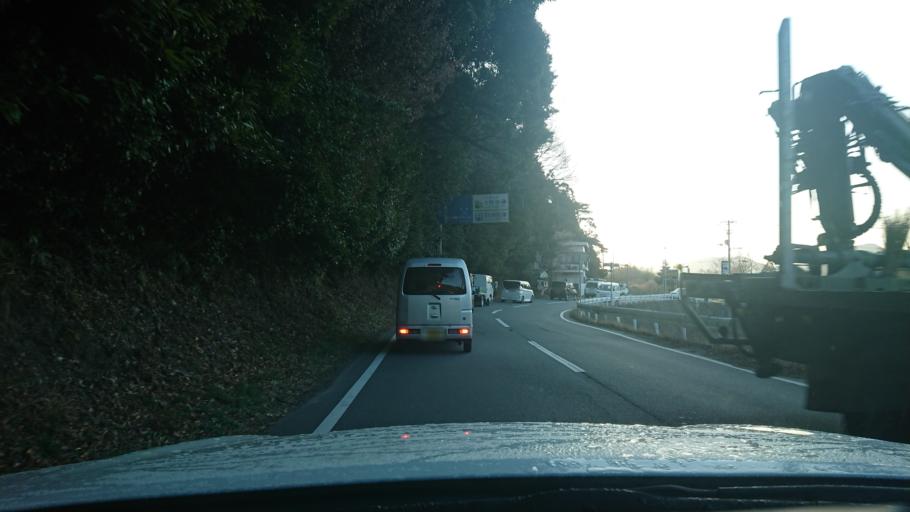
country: JP
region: Tokushima
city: Komatsushimacho
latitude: 33.9445
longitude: 134.5767
